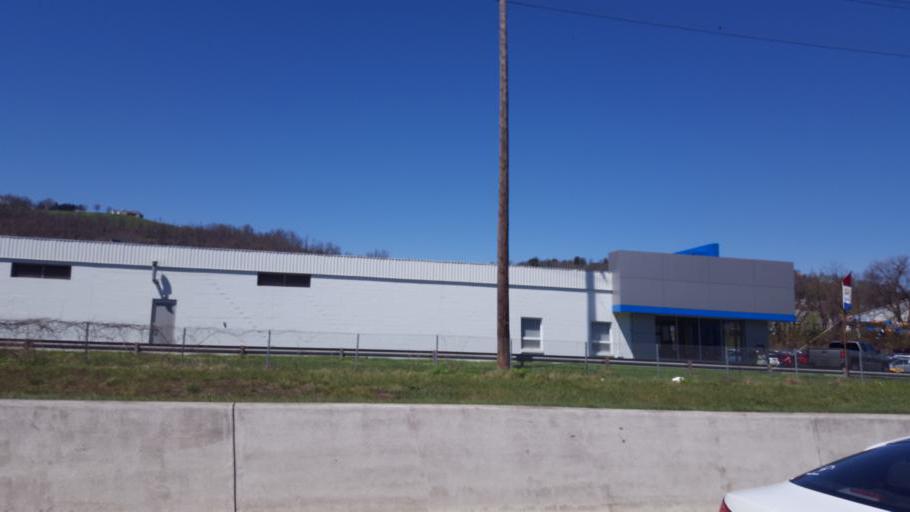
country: US
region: Ohio
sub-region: Belmont County
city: Martins Ferry
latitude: 40.0892
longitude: -80.7293
